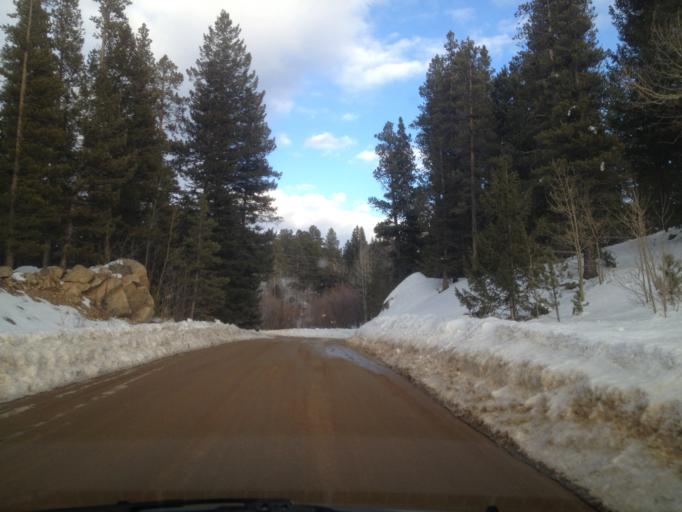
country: US
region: Colorado
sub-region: Boulder County
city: Nederland
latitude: 40.1238
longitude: -105.4390
